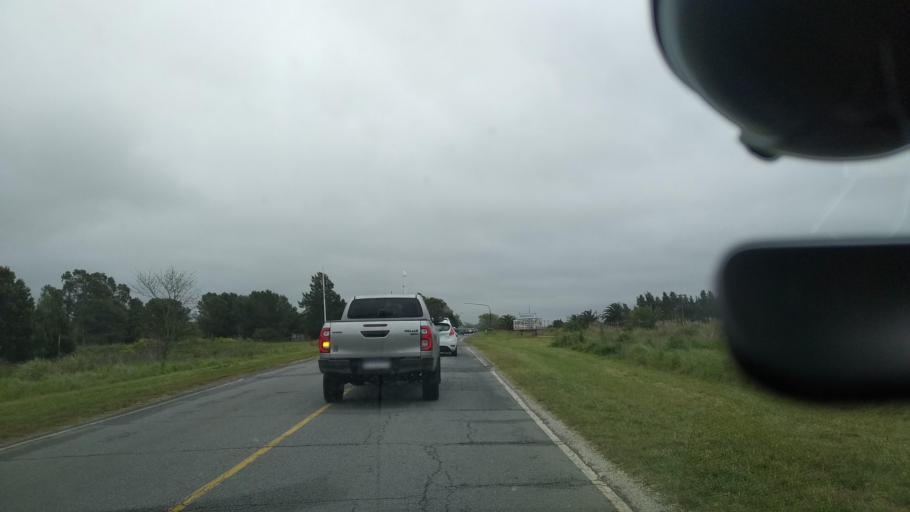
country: AR
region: Buenos Aires
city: Veronica
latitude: -35.5347
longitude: -57.3205
